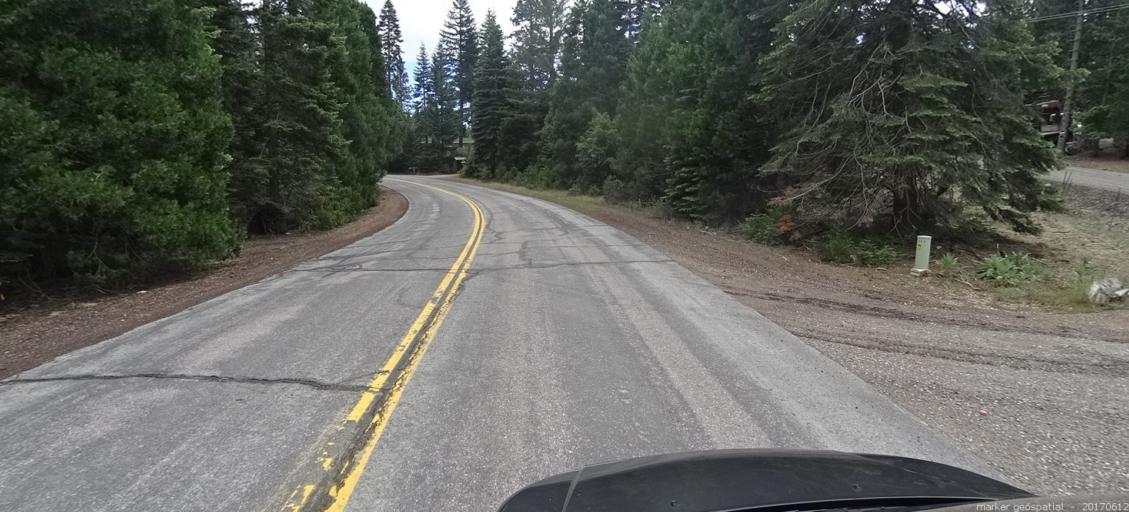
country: US
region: California
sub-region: Siskiyou County
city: Weed
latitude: 41.3587
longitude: -122.3649
